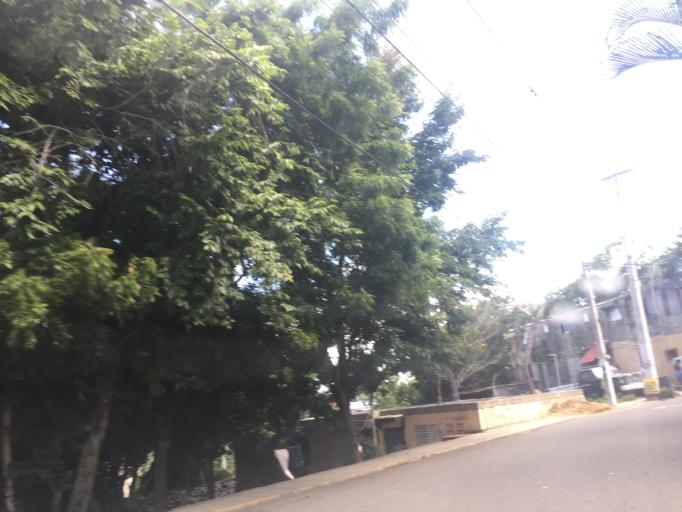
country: DO
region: Santiago
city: Santiago de los Caballeros
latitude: 19.4329
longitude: -70.6750
